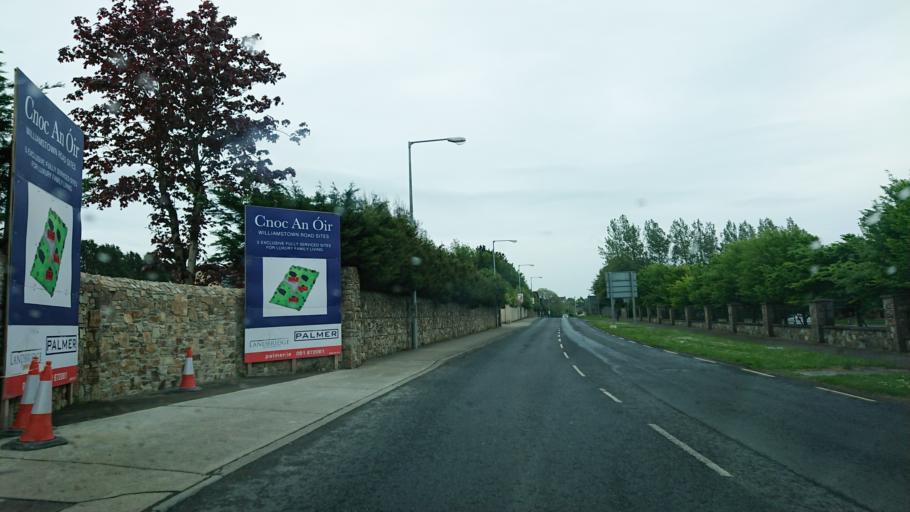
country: IE
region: Munster
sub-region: Waterford
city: Waterford
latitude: 52.2405
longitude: -7.0882
